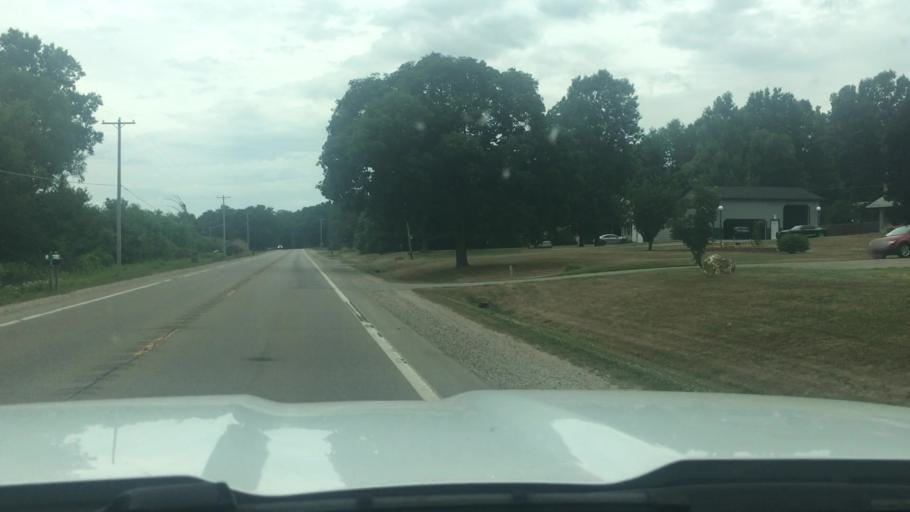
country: US
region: Michigan
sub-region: Kent County
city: Lowell
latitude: 42.9375
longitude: -85.3011
